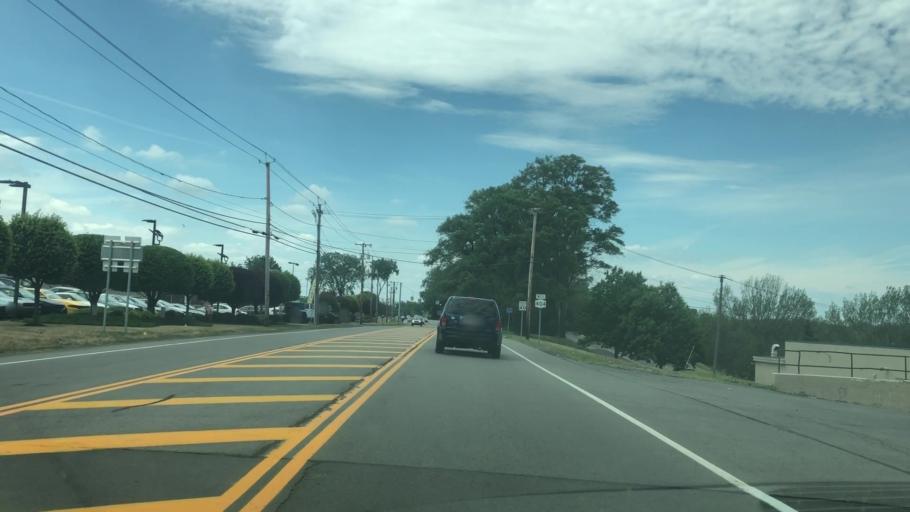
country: US
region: New York
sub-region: Monroe County
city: Webster
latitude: 43.2084
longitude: -77.4623
